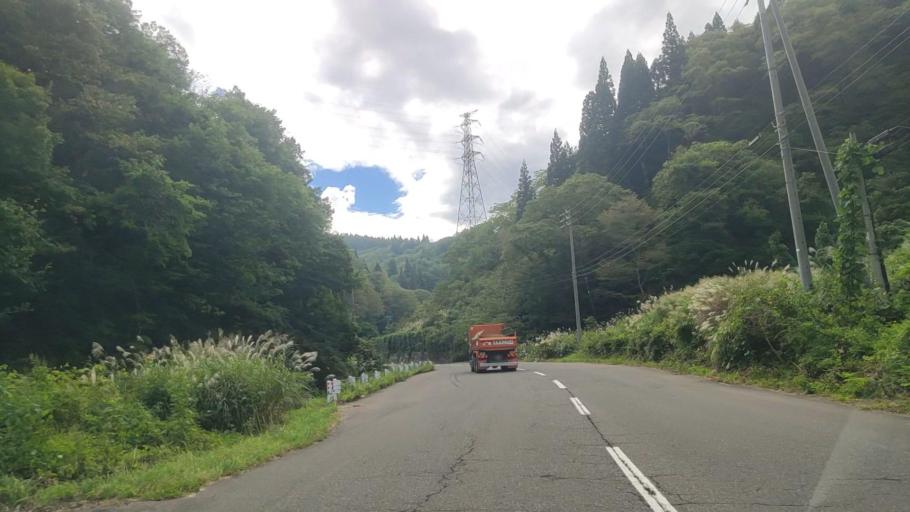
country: JP
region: Nagano
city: Iiyama
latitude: 36.8925
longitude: 138.3226
